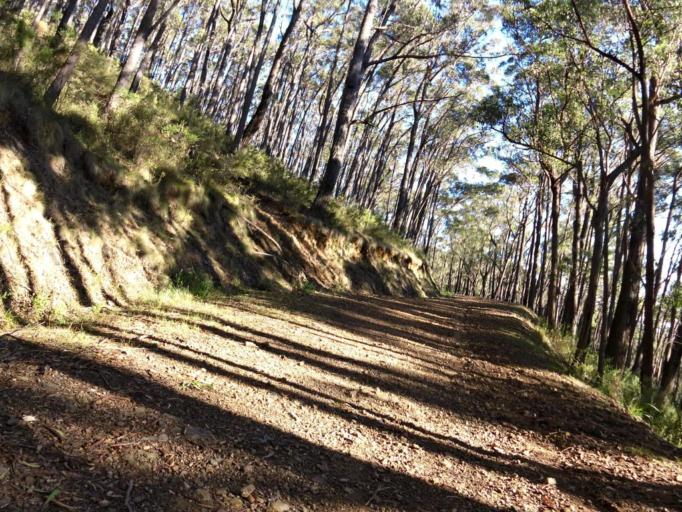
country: AU
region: Victoria
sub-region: Yarra Ranges
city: Millgrove
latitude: -37.7724
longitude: 145.6609
